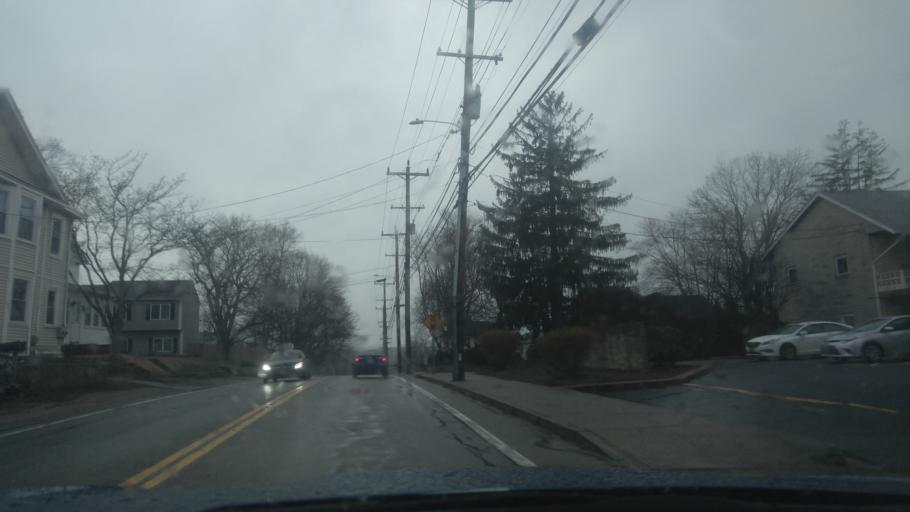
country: US
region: Rhode Island
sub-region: Kent County
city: West Warwick
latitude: 41.6846
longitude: -71.5175
